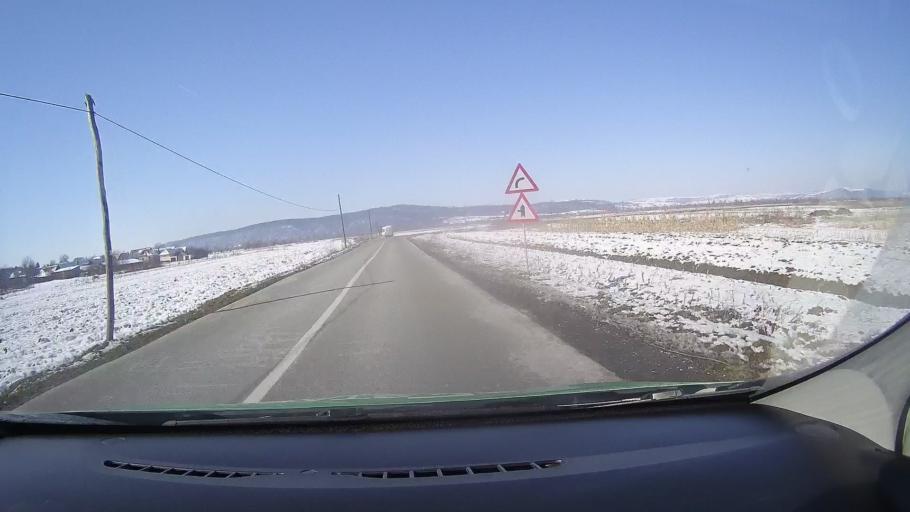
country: RO
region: Brasov
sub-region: Comuna Comana
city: Comana de Jos
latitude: 45.8784
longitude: 25.2124
